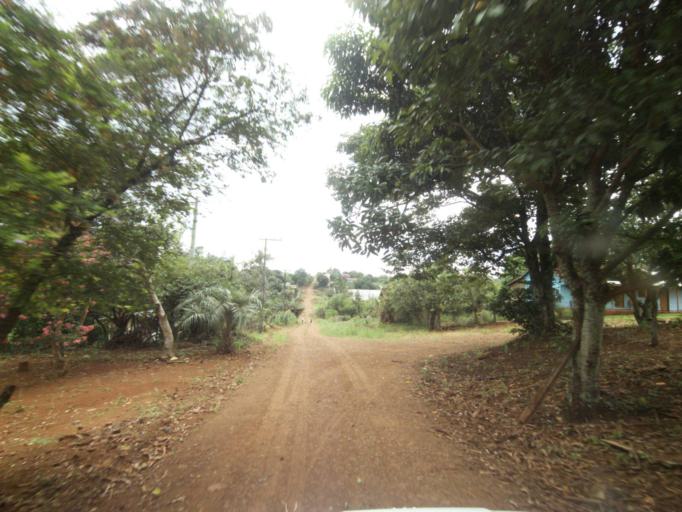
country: BR
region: Parana
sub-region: Guaraniacu
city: Guaraniacu
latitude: -24.9175
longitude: -52.9360
